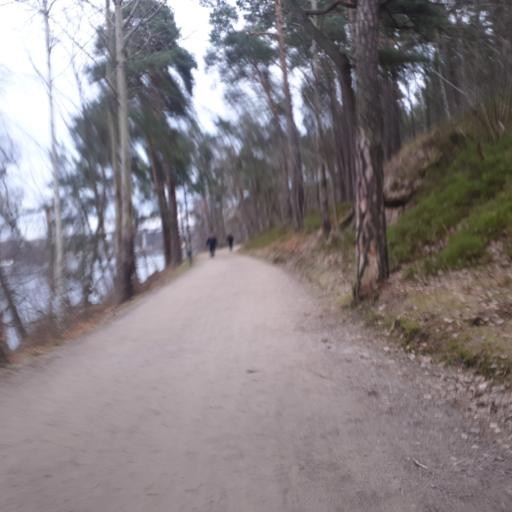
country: SE
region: Stockholm
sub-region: Stockholms Kommun
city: Arsta
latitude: 59.3028
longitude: 18.0613
